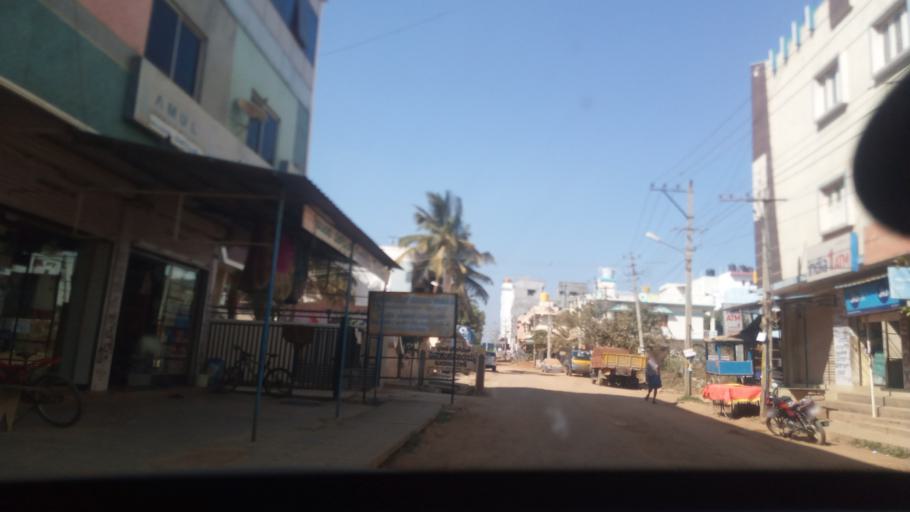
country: IN
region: Karnataka
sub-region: Bangalore Rural
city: Nelamangala
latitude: 13.0386
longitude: 77.4940
